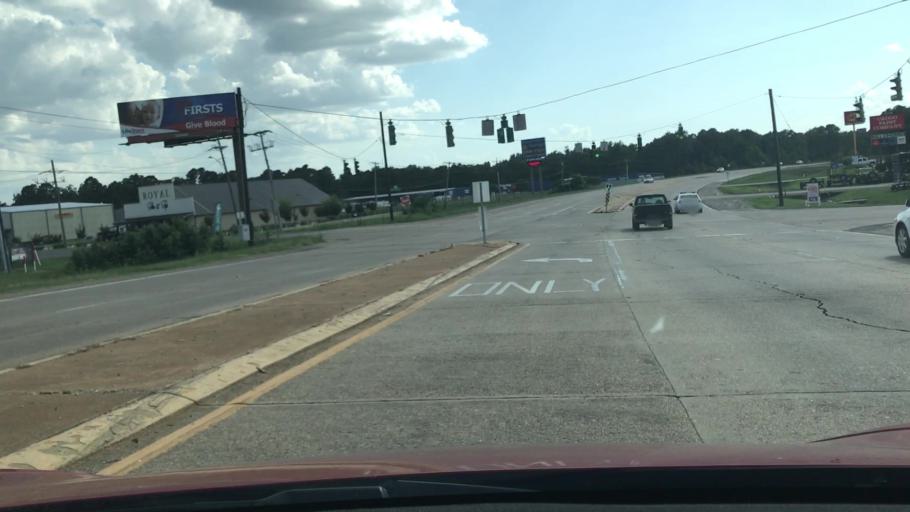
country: US
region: Louisiana
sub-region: Bossier Parish
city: Bossier City
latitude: 32.3996
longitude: -93.7381
